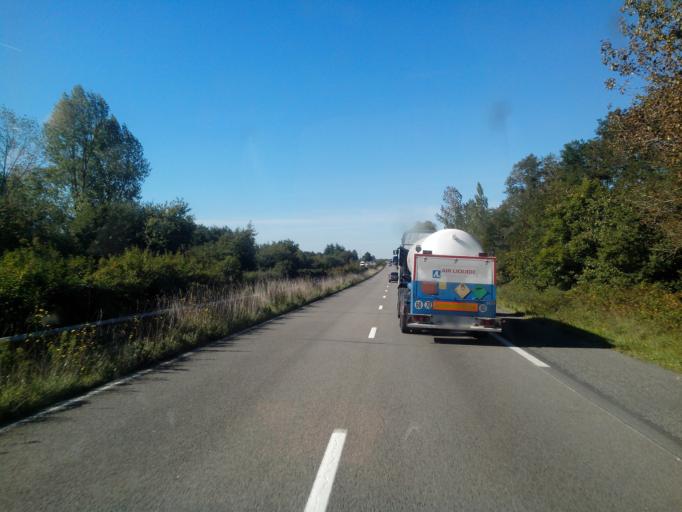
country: FR
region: Pays de la Loire
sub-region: Departement de la Loire-Atlantique
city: Missillac
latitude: 47.4626
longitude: -2.1510
